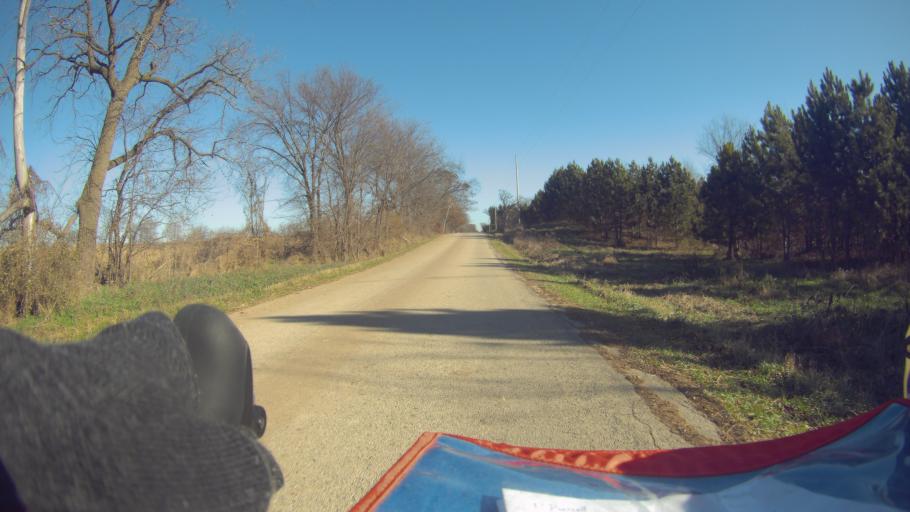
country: US
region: Wisconsin
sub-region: Green County
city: Brooklyn
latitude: 42.8384
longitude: -89.3481
